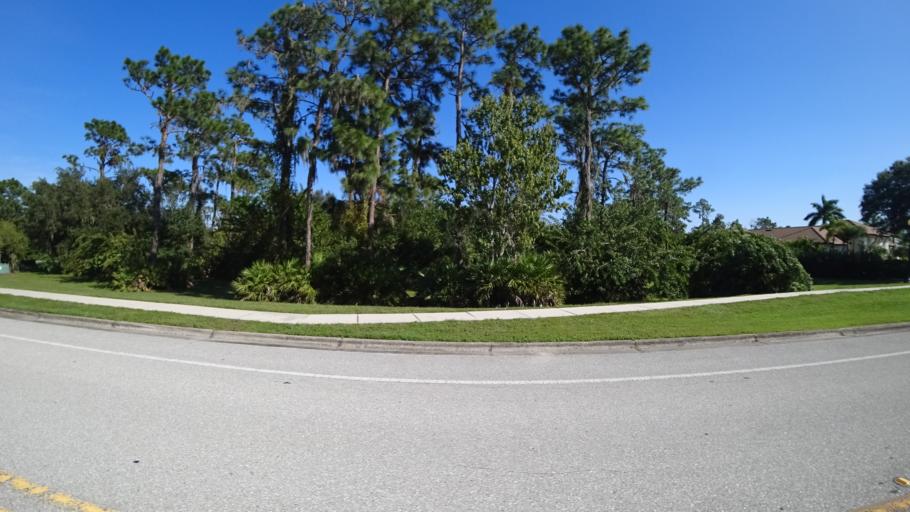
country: US
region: Florida
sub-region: Sarasota County
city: The Meadows
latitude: 27.4167
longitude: -82.4366
